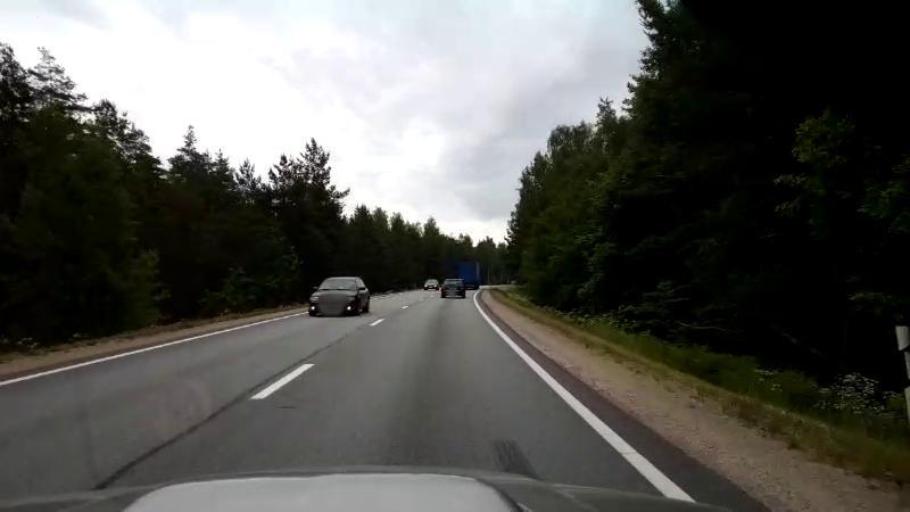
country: LV
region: Riga
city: Bergi
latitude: 56.9637
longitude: 24.3700
